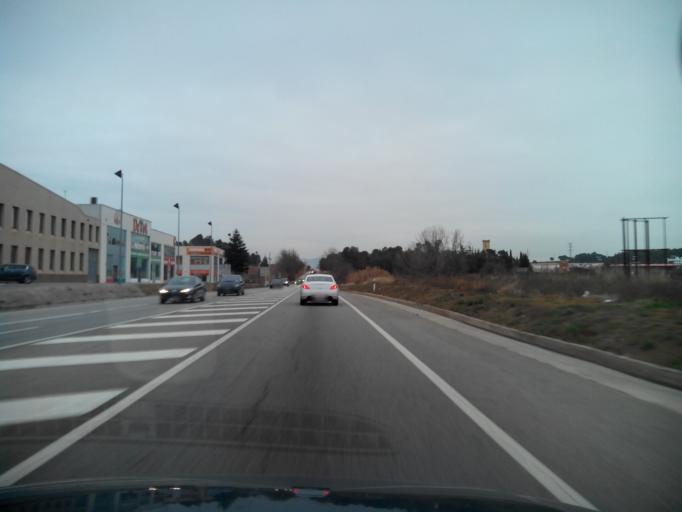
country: ES
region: Catalonia
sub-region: Provincia de Barcelona
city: Sant Fruitos de Bages
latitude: 41.7517
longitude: 1.8637
